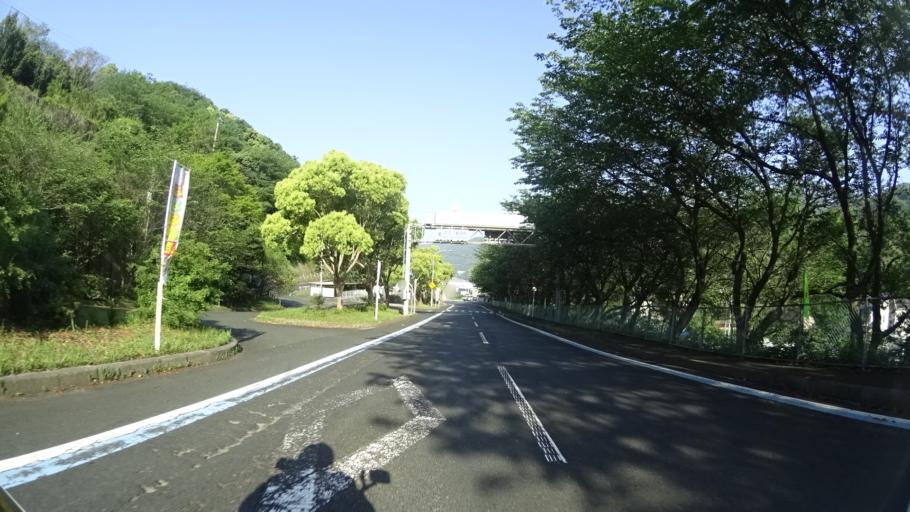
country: JP
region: Ehime
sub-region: Nishiuwa-gun
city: Ikata-cho
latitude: 33.3867
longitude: 132.1300
